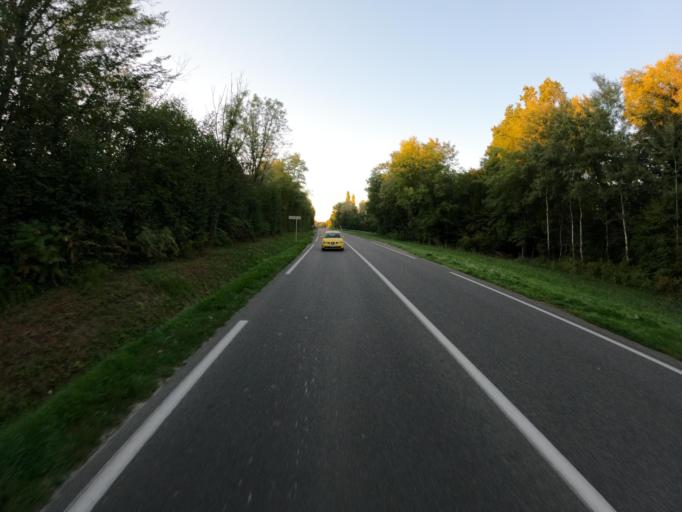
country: FR
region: Franche-Comte
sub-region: Departement du Jura
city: Bletterans
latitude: 46.7055
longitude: 5.4828
